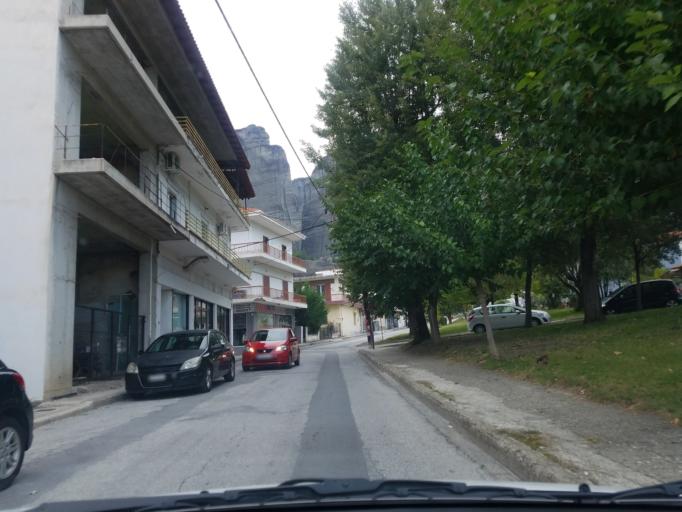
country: GR
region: Thessaly
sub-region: Trikala
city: Kalampaka
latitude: 39.7062
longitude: 21.6303
